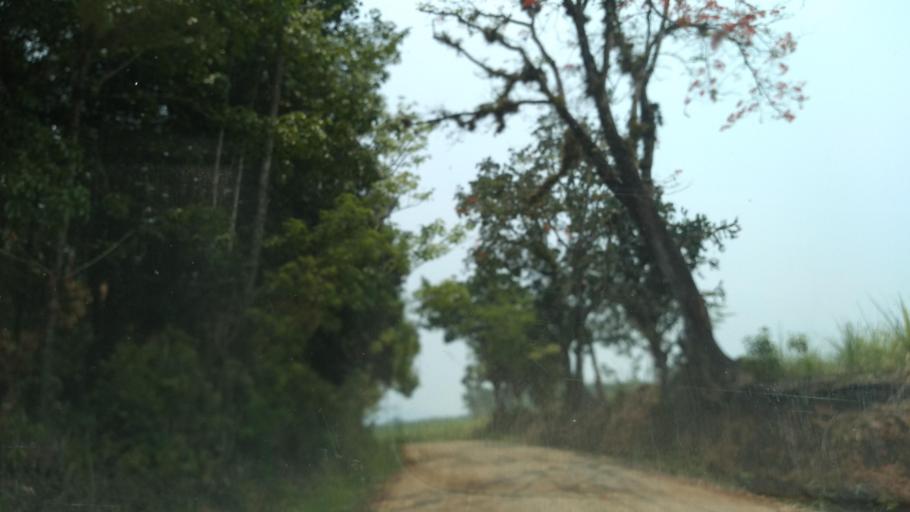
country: MX
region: Veracruz
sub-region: Tezonapa
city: Laguna Chica (Pueblo Nuevo)
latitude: 18.5058
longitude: -96.7711
